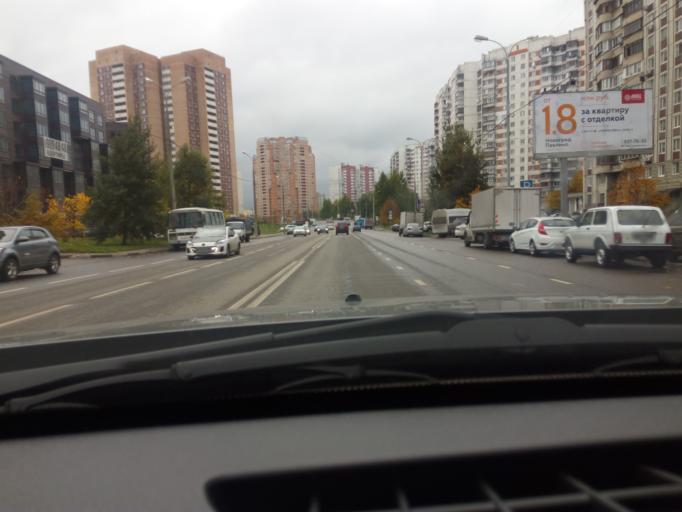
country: RU
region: Moskovskaya
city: Reutov
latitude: 55.7402
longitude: 37.8597
